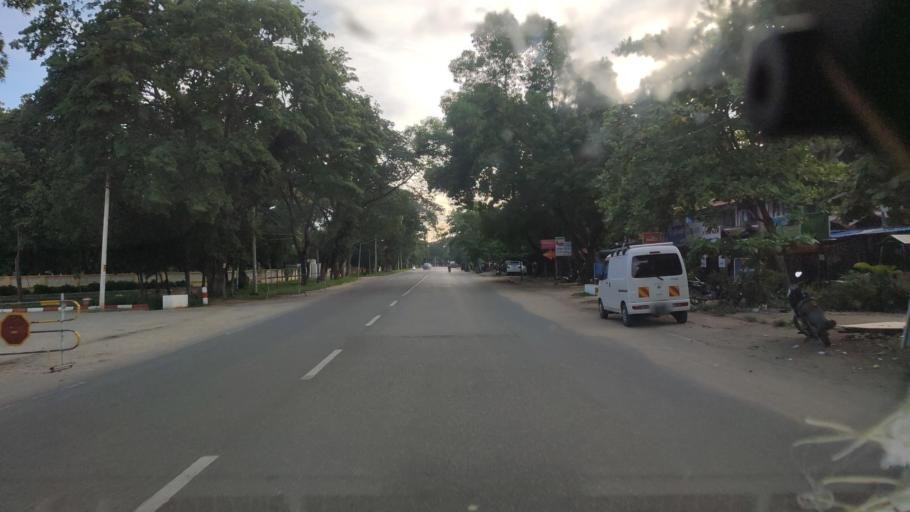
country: MM
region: Magway
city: Magway
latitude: 20.1399
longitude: 94.9355
